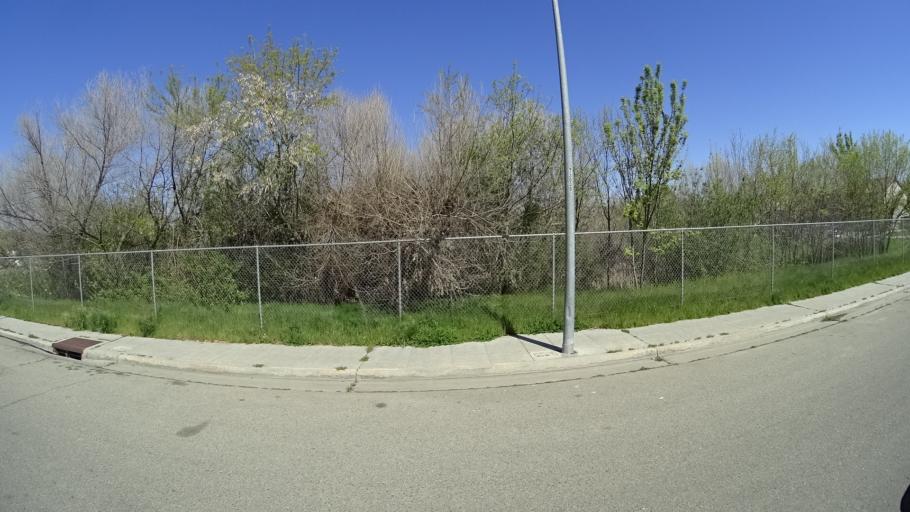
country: US
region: California
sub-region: Fresno County
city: West Park
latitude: 36.7830
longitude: -119.8905
